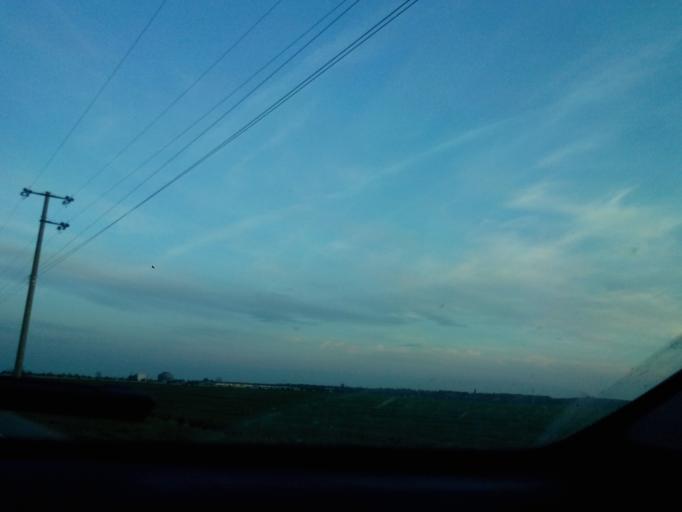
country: RO
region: Prahova
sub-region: Oras Baicoi
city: Tintea
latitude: 44.9927
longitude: 25.9067
